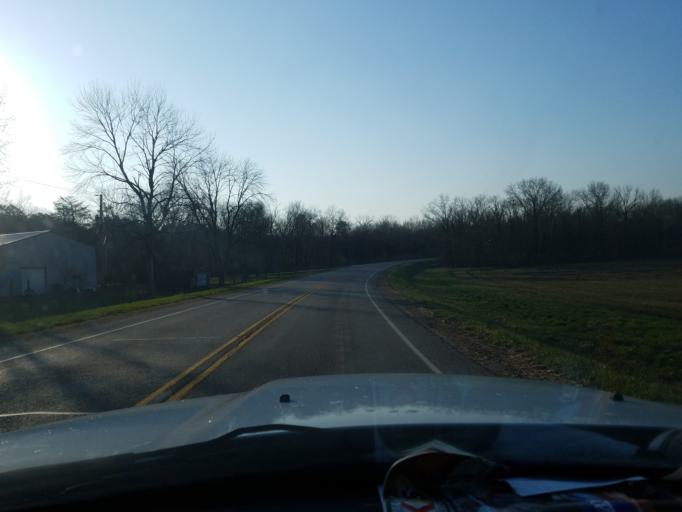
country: US
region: Indiana
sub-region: Vigo County
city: Seelyville
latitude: 39.4068
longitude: -87.3237
